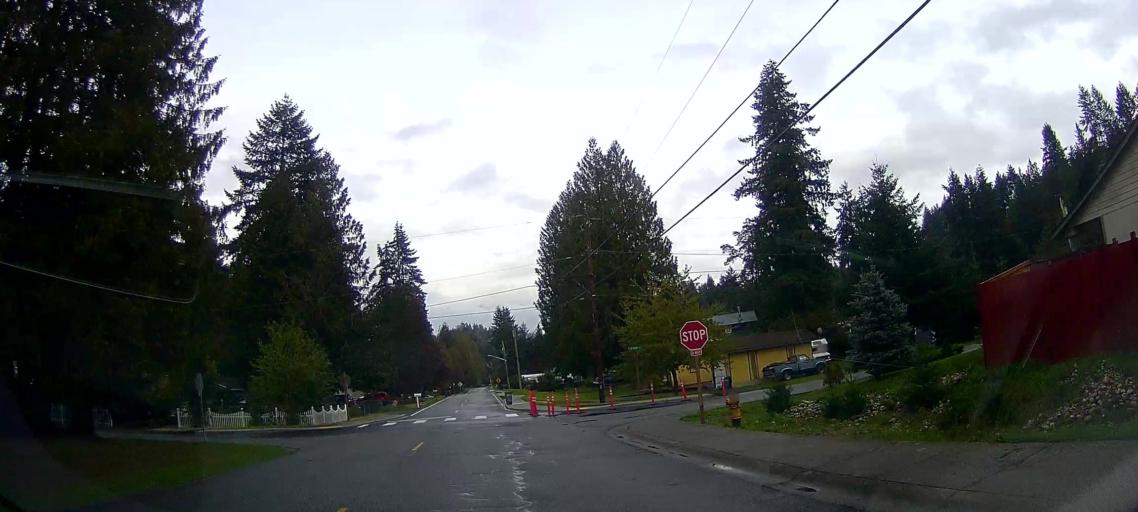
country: US
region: Washington
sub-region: Snohomish County
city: Darrington
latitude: 48.5346
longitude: -121.7632
